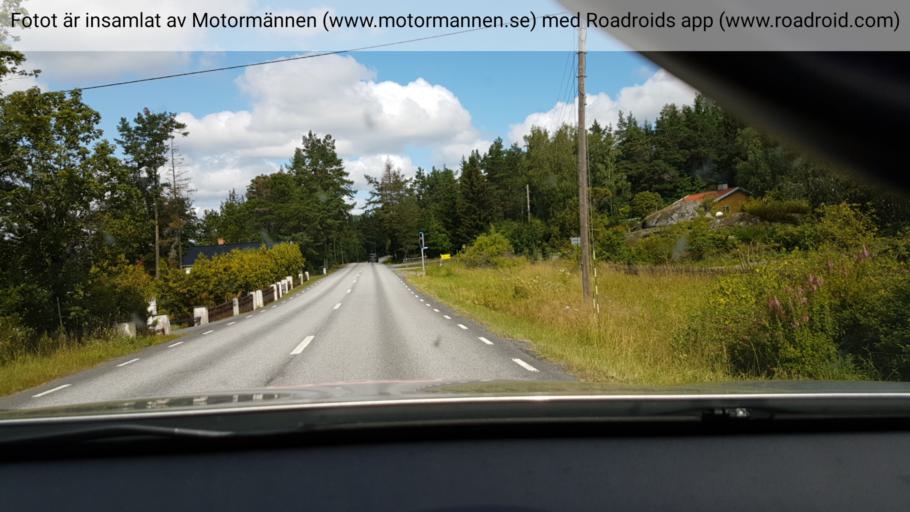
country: SE
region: Stockholm
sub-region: Norrtalje Kommun
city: Arno
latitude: 60.0481
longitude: 18.7721
